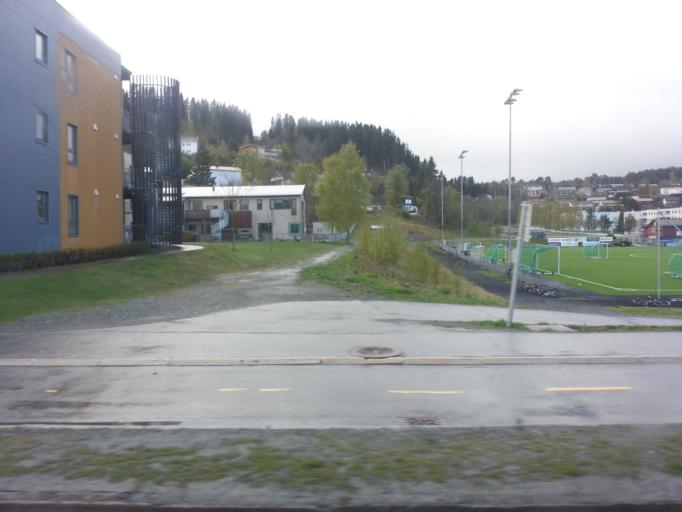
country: NO
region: Sor-Trondelag
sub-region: Trondheim
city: Trondheim
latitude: 63.4049
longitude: 10.3588
